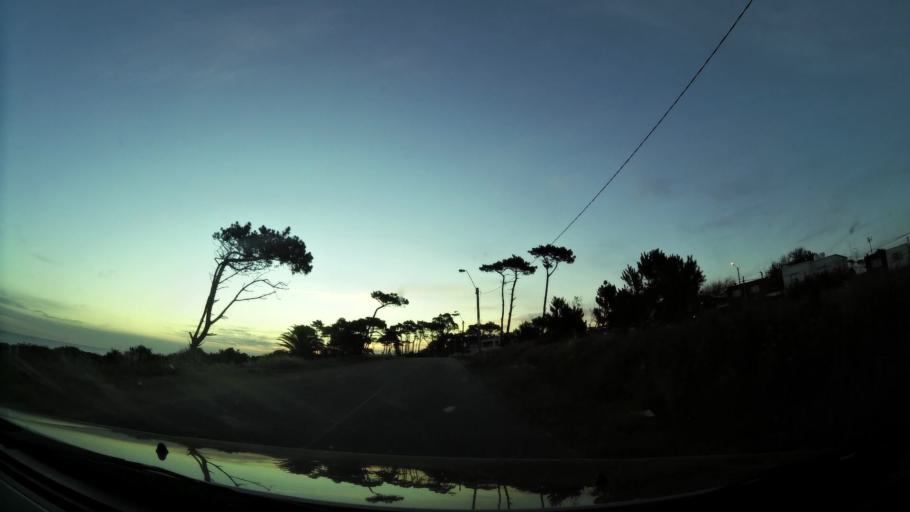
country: UY
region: Canelones
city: Atlantida
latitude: -34.7772
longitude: -55.7446
